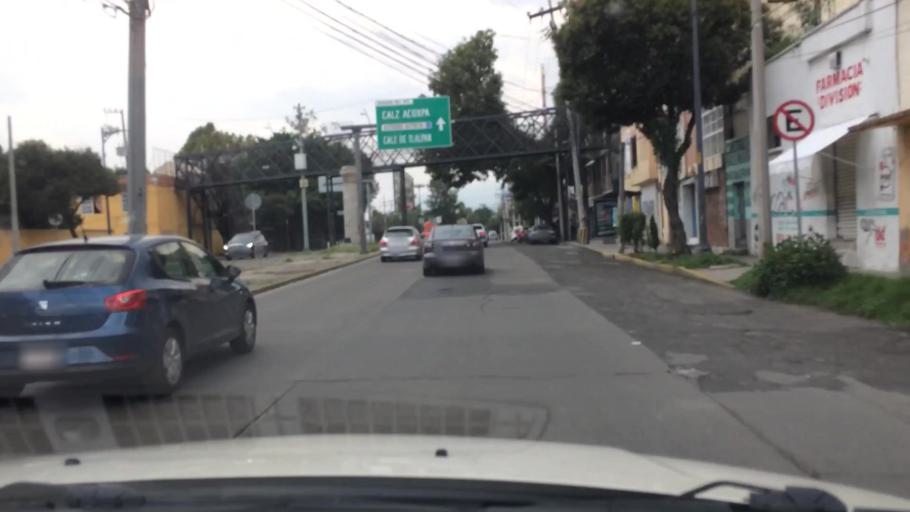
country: MX
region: Mexico City
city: Coyoacan
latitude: 19.3232
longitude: -99.1394
